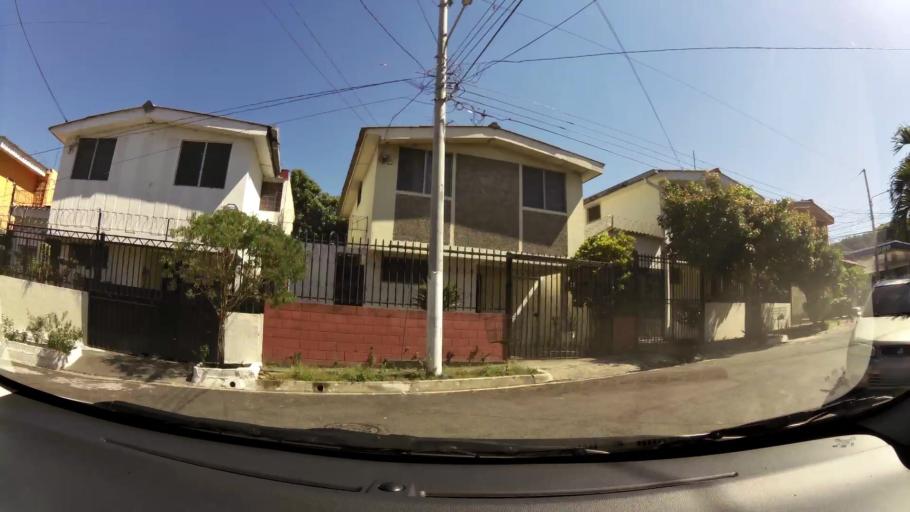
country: SV
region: La Libertad
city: Santa Tecla
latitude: 13.6740
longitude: -89.3004
